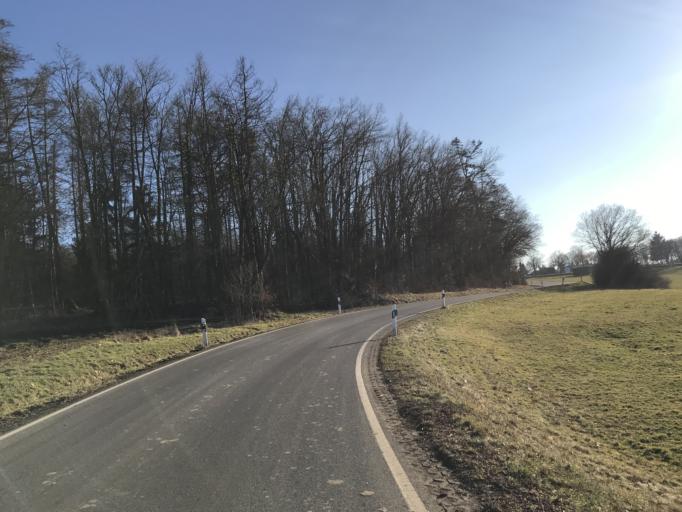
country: DE
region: Hesse
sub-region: Regierungsbezirk Giessen
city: Rabenau
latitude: 50.6626
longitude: 8.8524
